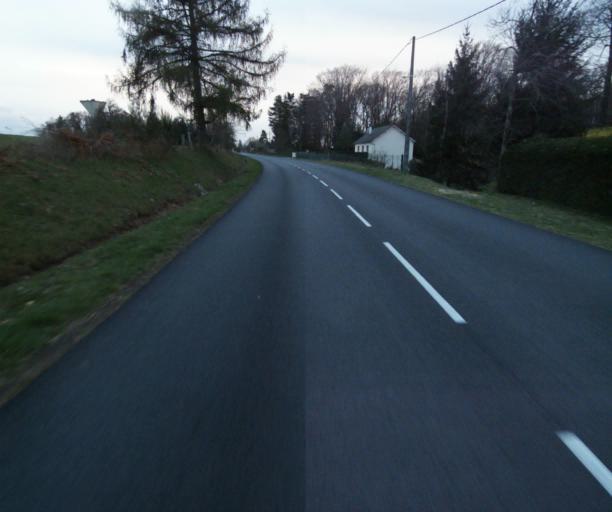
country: FR
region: Limousin
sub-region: Departement de la Correze
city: Correze
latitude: 45.3454
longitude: 1.8752
